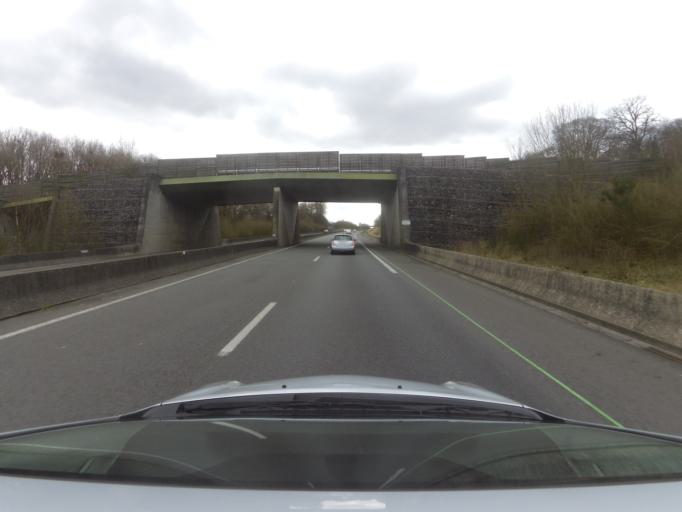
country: FR
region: Nord-Pas-de-Calais
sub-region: Departement du Pas-de-Calais
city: Saint-Josse
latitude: 50.4777
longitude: 1.6968
